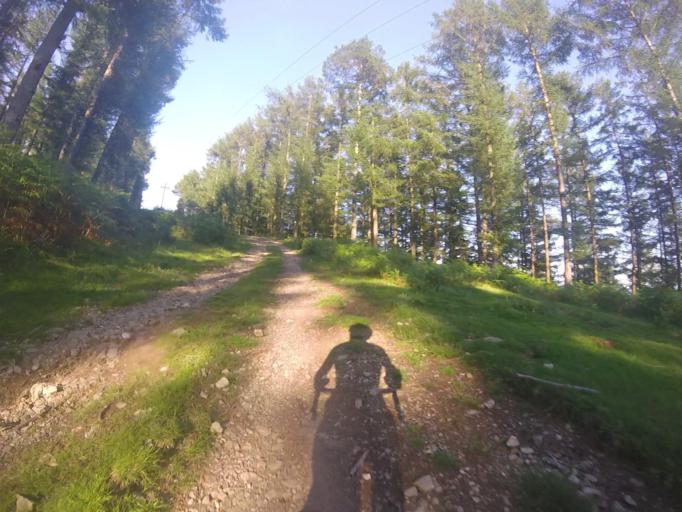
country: ES
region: Navarre
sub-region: Provincia de Navarra
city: Arano
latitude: 43.2424
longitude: -1.8535
